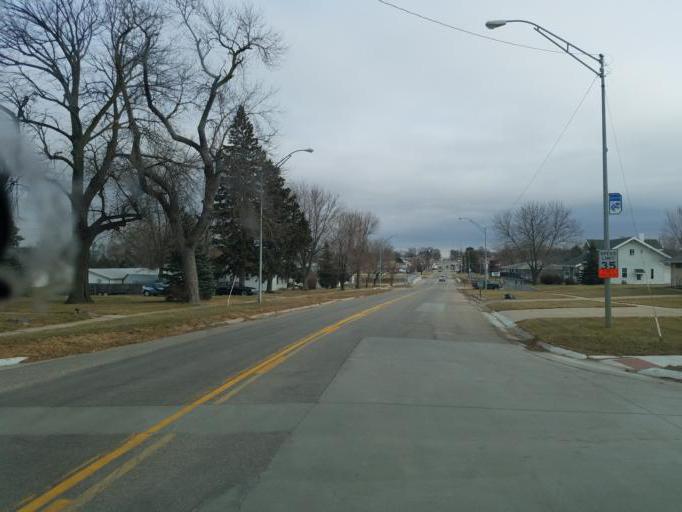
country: US
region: Nebraska
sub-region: Knox County
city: Bloomfield
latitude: 42.5997
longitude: -97.6525
